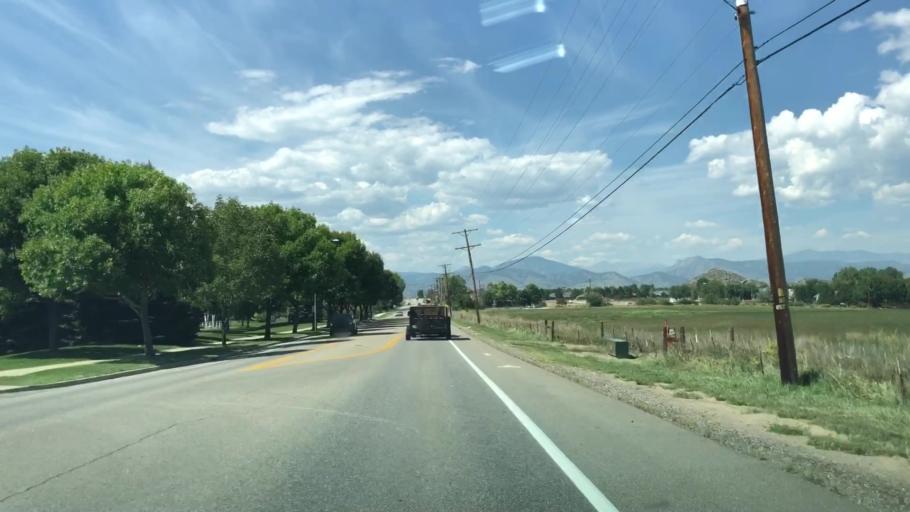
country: US
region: Colorado
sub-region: Larimer County
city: Loveland
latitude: 40.3930
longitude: -105.1212
